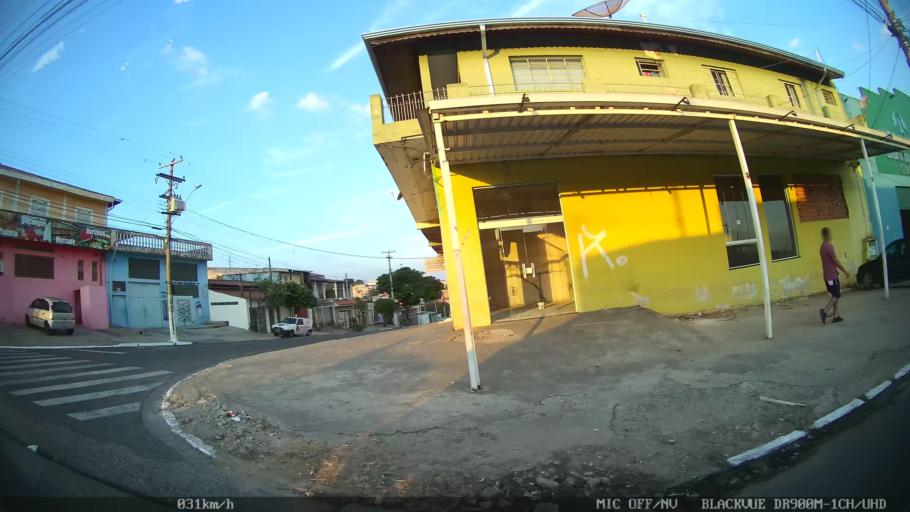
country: BR
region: Sao Paulo
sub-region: Hortolandia
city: Hortolandia
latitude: -22.8550
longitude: -47.2059
